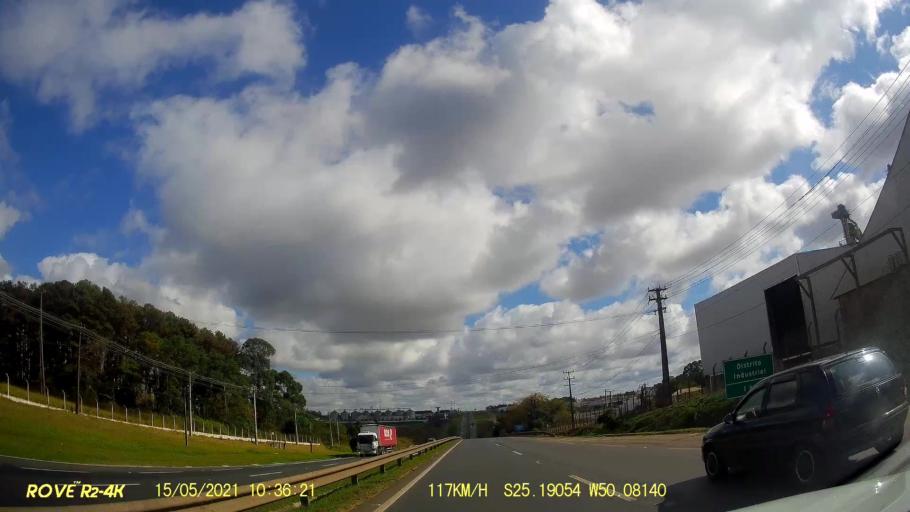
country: BR
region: Parana
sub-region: Ponta Grossa
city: Ponta Grossa
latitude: -25.1904
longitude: -50.0809
